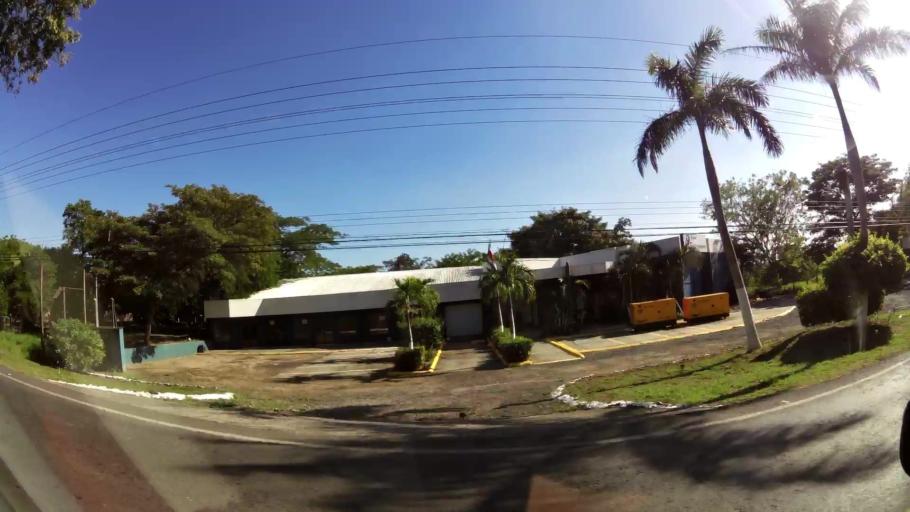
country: CR
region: Guanacaste
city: Sardinal
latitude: 10.5812
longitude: -85.5701
